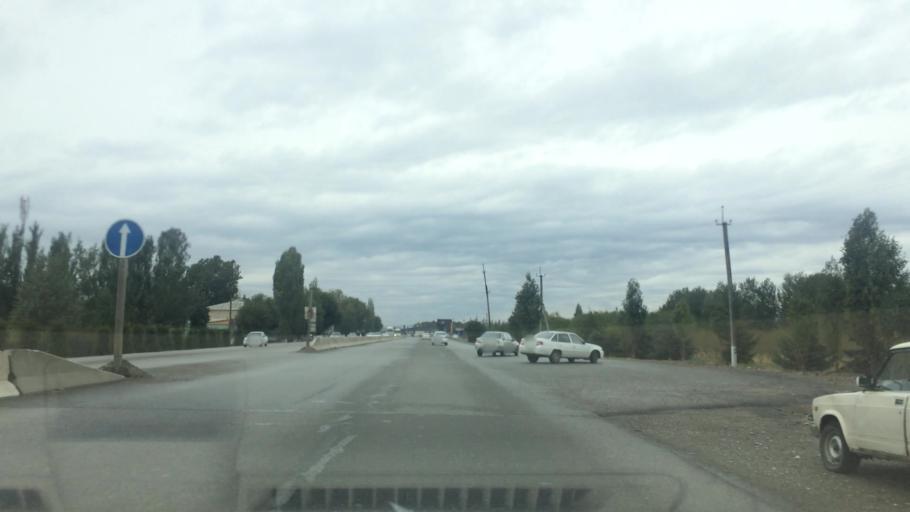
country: UZ
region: Jizzax
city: Jizzax
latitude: 40.0140
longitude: 67.6040
